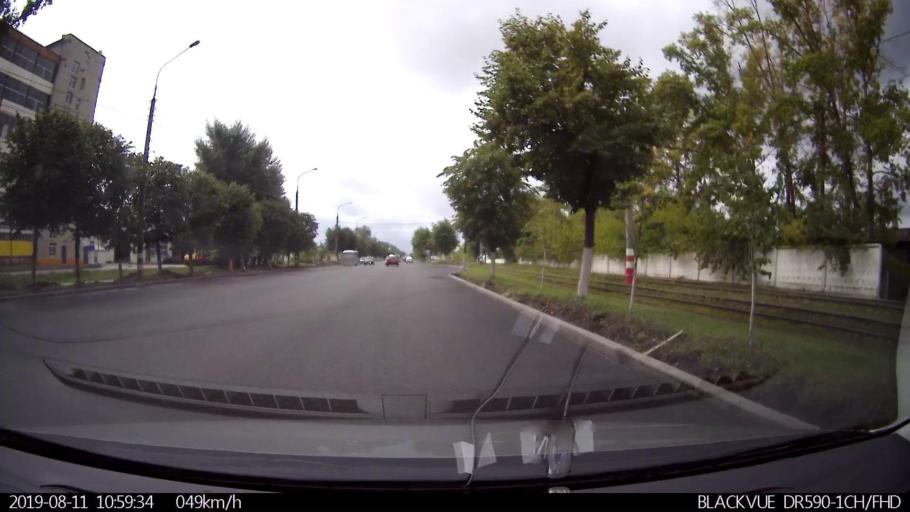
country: RU
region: Ulyanovsk
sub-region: Ulyanovskiy Rayon
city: Ulyanovsk
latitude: 54.2493
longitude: 48.3147
